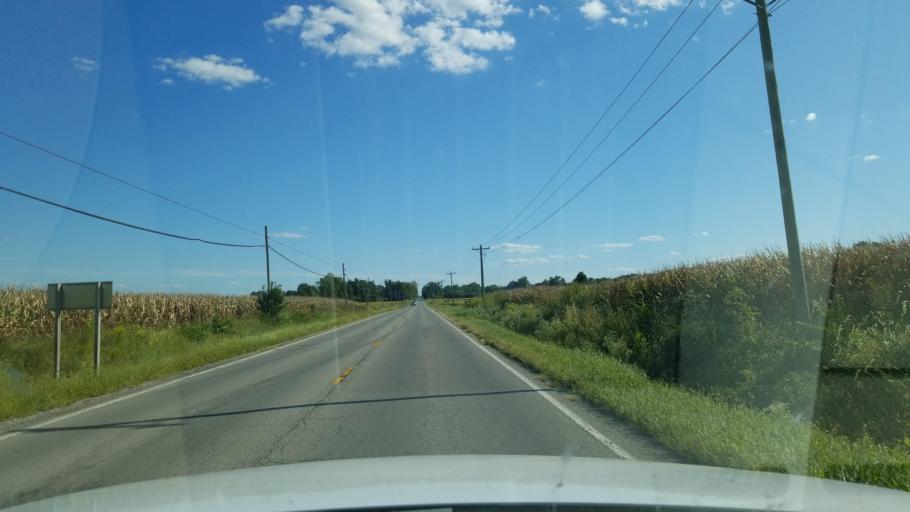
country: US
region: Illinois
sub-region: Saline County
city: Harrisburg
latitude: 37.6854
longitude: -88.5363
